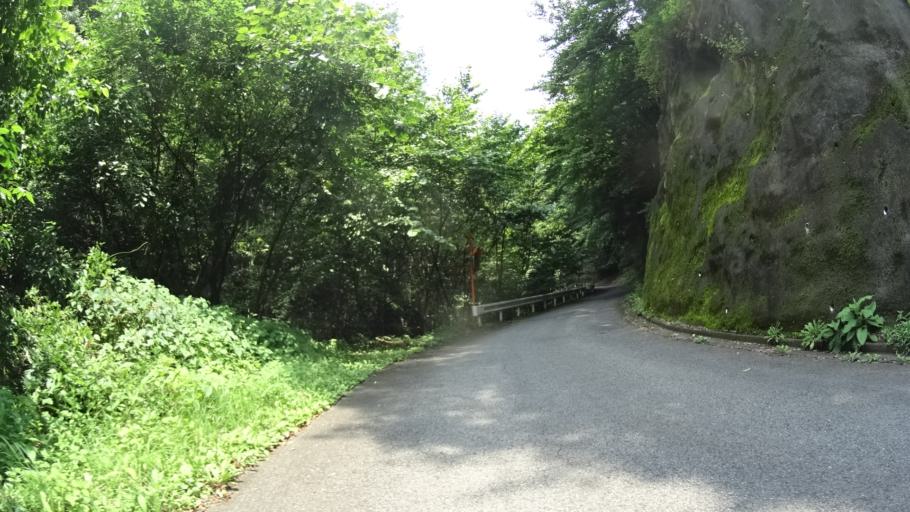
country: JP
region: Gunma
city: Tomioka
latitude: 36.0831
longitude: 138.7077
